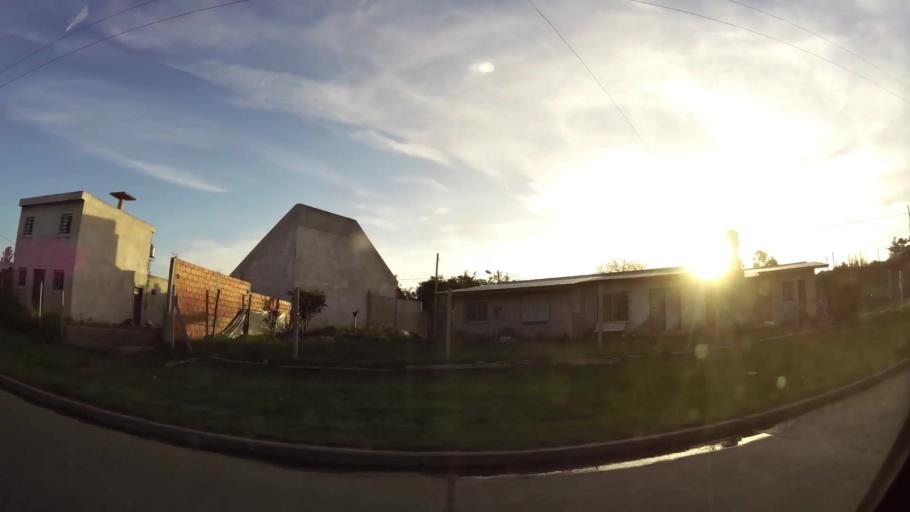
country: AR
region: Buenos Aires
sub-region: Partido de Quilmes
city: Quilmes
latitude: -34.7835
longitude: -58.1894
